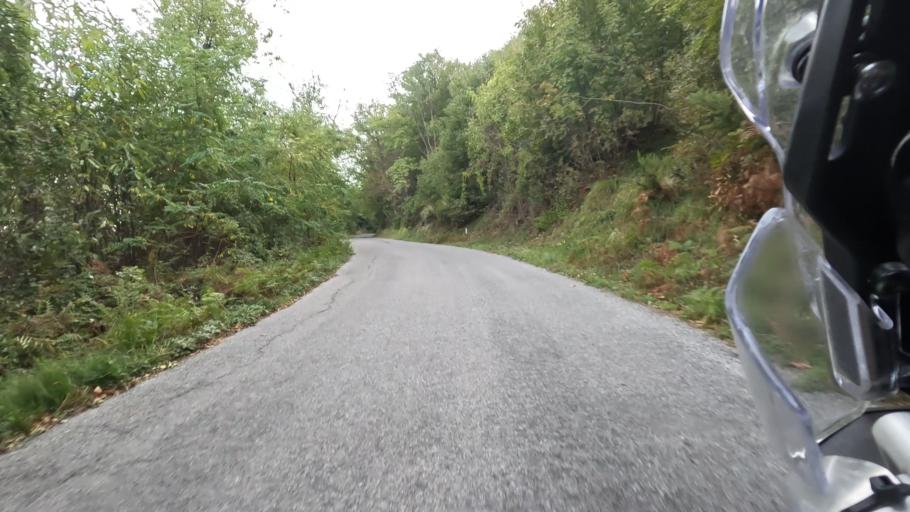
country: IT
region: Liguria
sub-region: Provincia di Savona
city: San Giovanni
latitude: 44.3952
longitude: 8.5349
